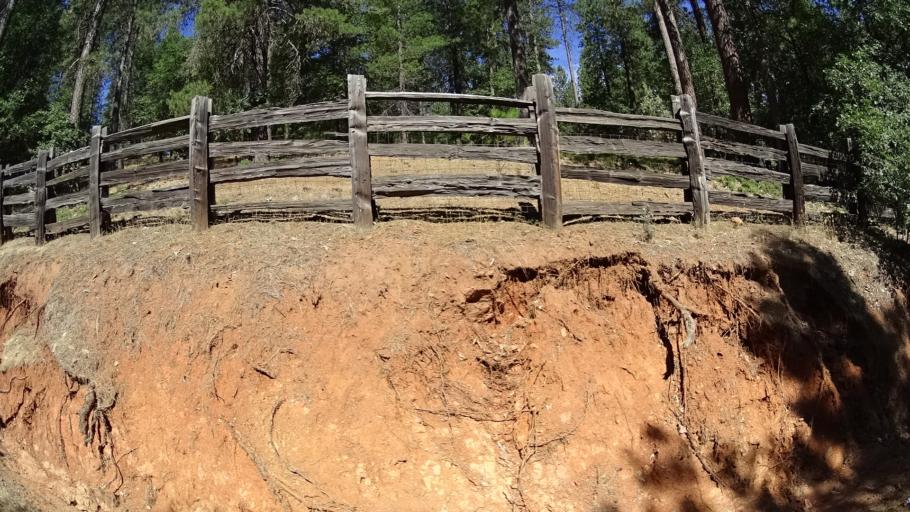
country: US
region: California
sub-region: Amador County
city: Pioneer
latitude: 38.3407
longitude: -120.5145
